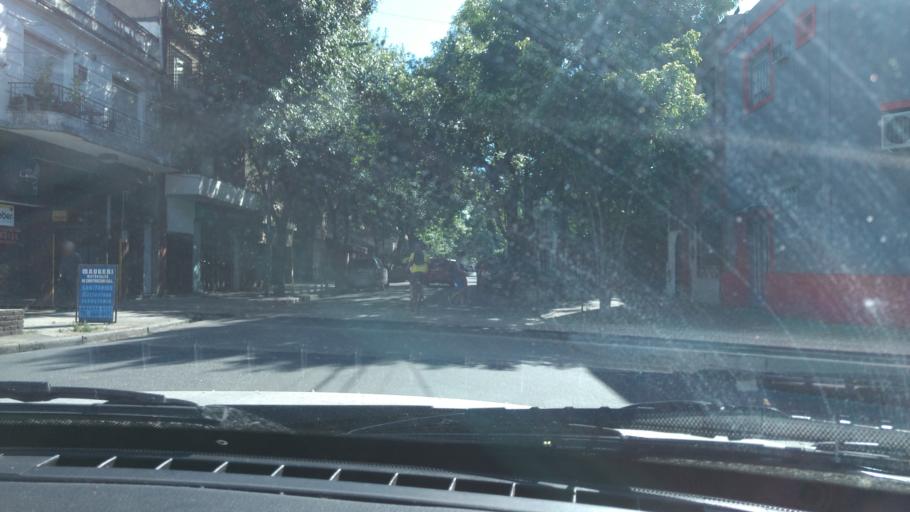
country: AR
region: Buenos Aires
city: Caseros
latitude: -34.6261
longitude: -58.5279
